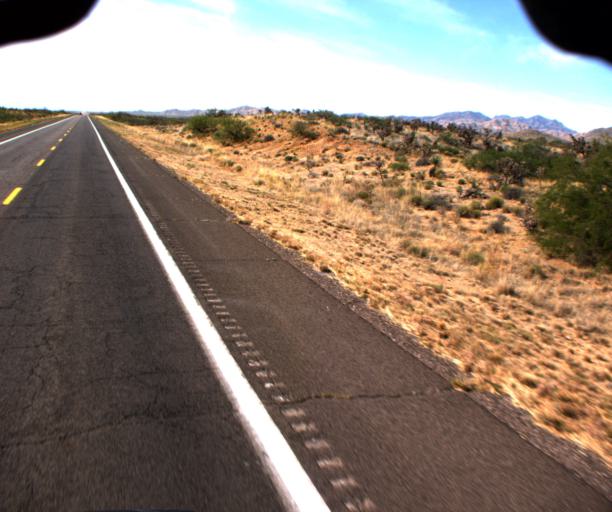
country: US
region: Arizona
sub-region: Graham County
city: Swift Trail Junction
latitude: 32.6152
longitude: -109.6881
